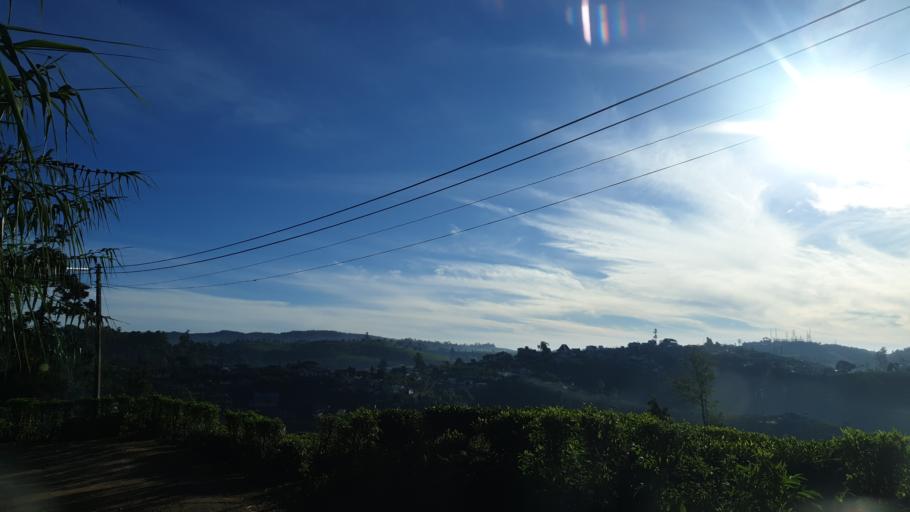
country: LK
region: Central
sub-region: Nuwara Eliya District
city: Nuwara Eliya
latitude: 6.9563
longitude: 80.7671
